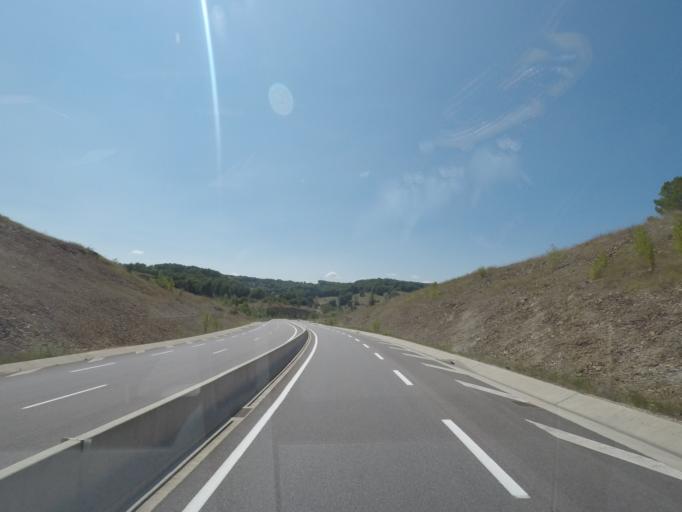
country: FR
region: Midi-Pyrenees
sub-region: Departement du Lot
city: Figeac
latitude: 44.5919
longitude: 2.0087
